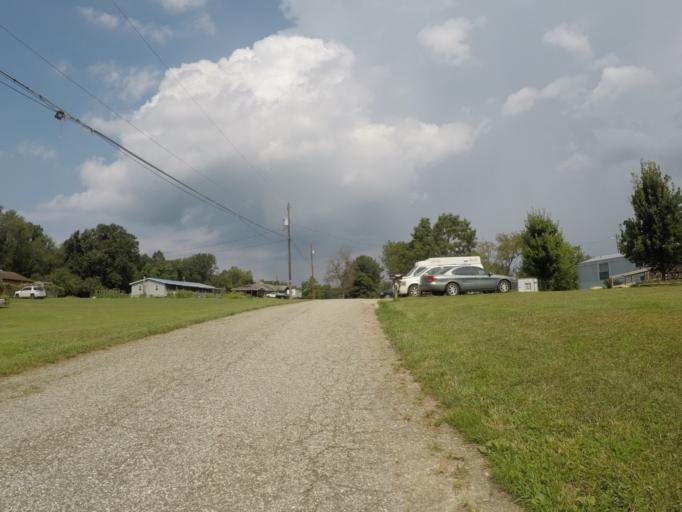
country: US
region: Kentucky
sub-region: Boyd County
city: Ironville
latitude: 38.4431
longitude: -82.7061
